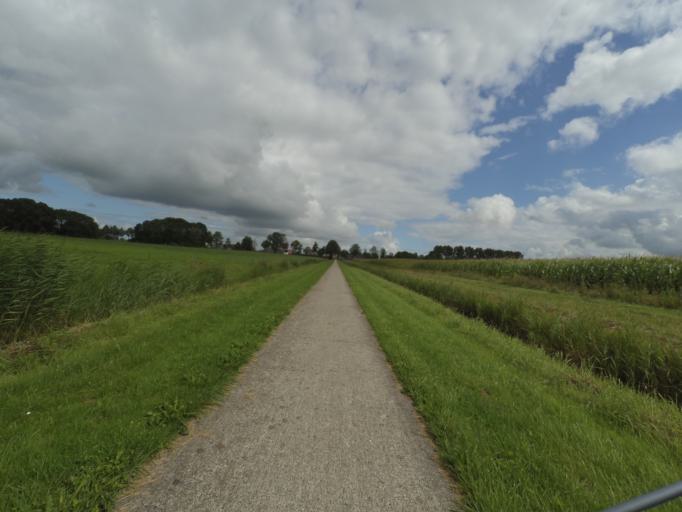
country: NL
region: Friesland
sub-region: Gemeente Kollumerland en Nieuwkruisland
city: Kollum
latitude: 53.2927
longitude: 6.2312
